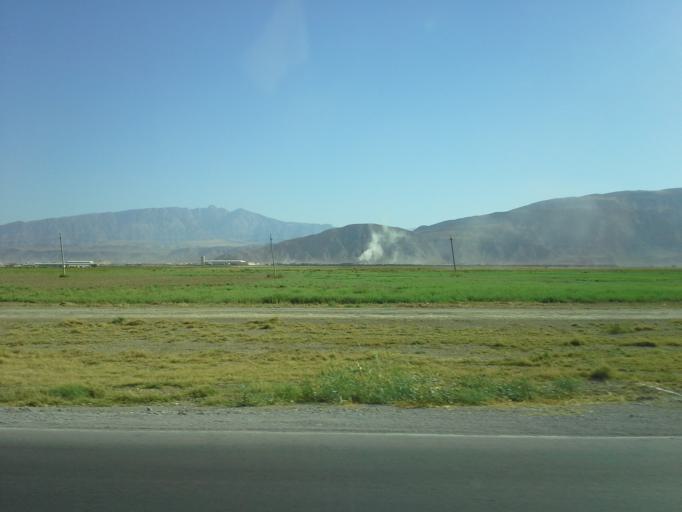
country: TM
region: Ahal
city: Abadan
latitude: 38.1698
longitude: 57.9190
